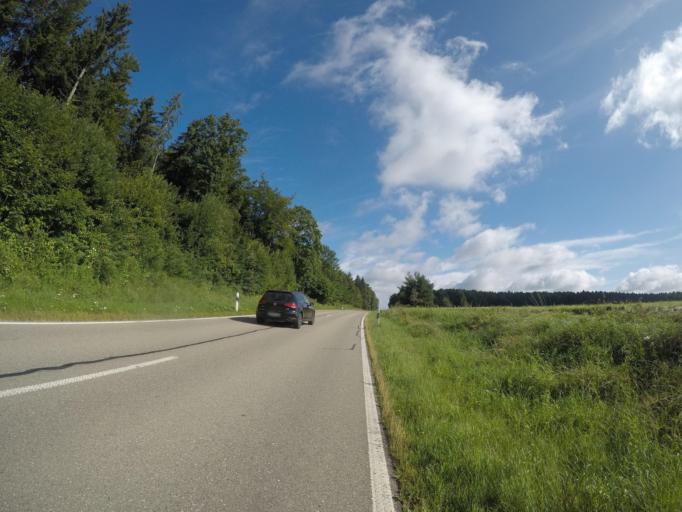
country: DE
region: Baden-Wuerttemberg
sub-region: Tuebingen Region
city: Laichingen
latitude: 48.4136
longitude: 9.6497
